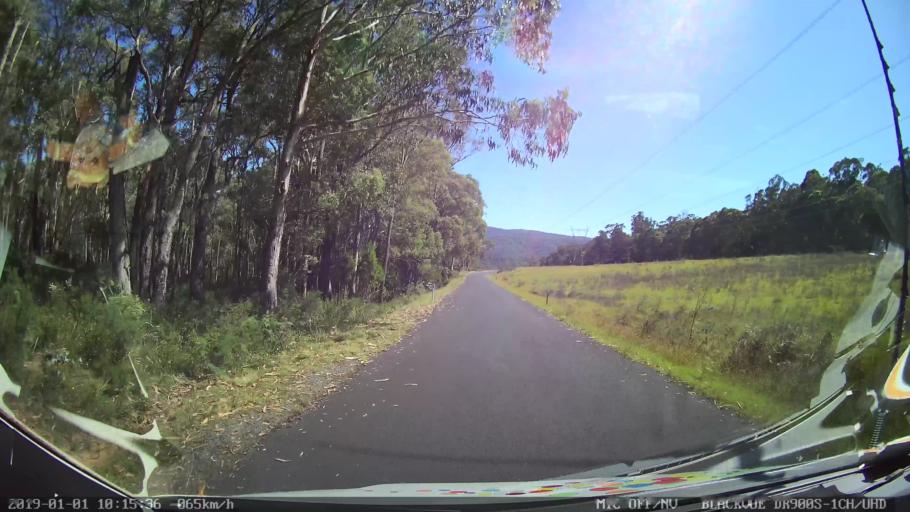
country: AU
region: New South Wales
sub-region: Snowy River
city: Jindabyne
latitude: -36.1000
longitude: 148.1621
